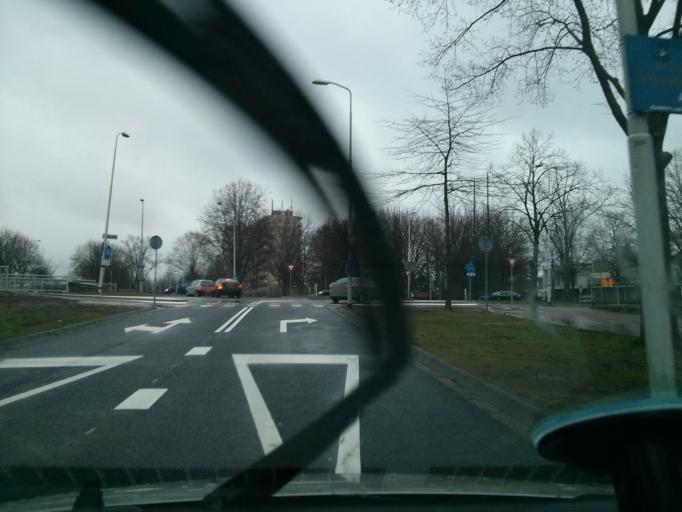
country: NL
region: North Brabant
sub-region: Gemeente Eindhoven
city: Villapark
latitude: 51.4754
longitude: 5.4890
